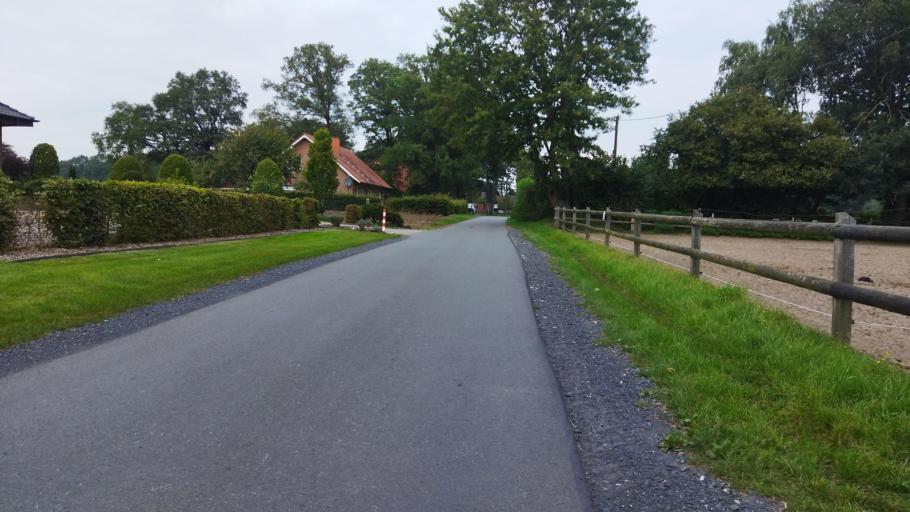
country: DE
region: North Rhine-Westphalia
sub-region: Regierungsbezirk Munster
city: Telgte
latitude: 52.0052
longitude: 7.7685
